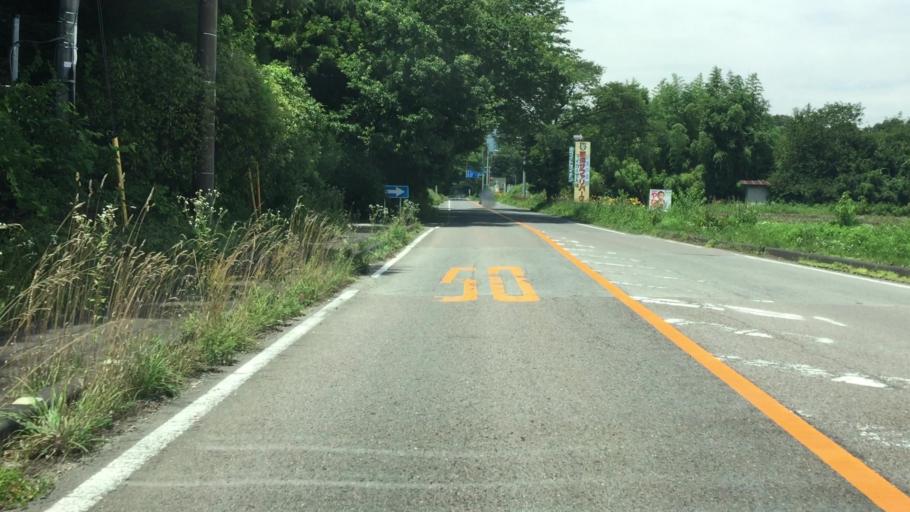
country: JP
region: Tochigi
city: Kuroiso
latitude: 37.0135
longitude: 139.9616
